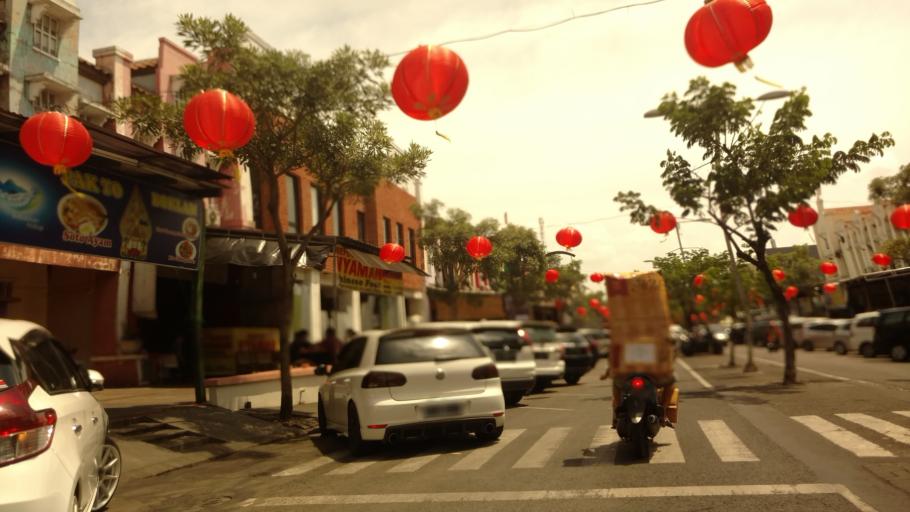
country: ID
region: East Java
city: Driyorejo
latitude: -7.2883
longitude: 112.6554
